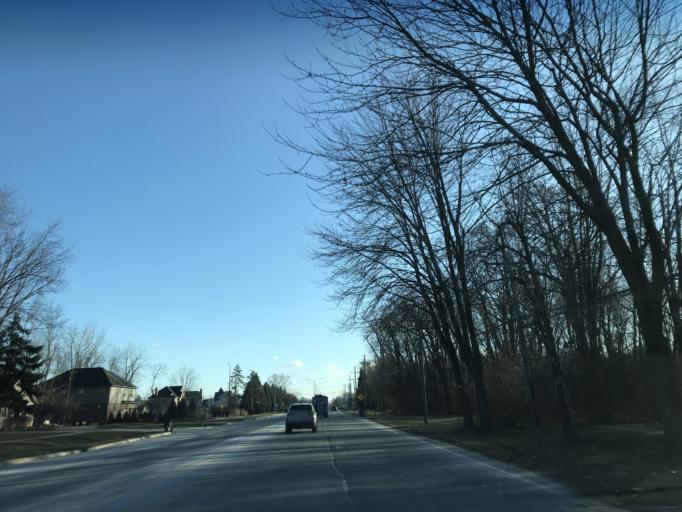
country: US
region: Michigan
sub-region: Oakland County
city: Troy
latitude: 42.5776
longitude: -83.1346
